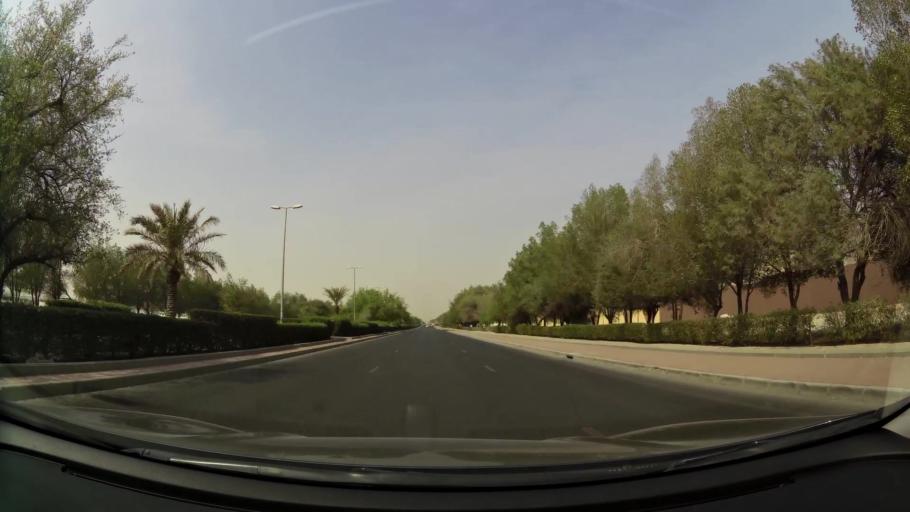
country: KW
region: Al Farwaniyah
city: Al Farwaniyah
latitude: 29.2496
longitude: 47.9269
